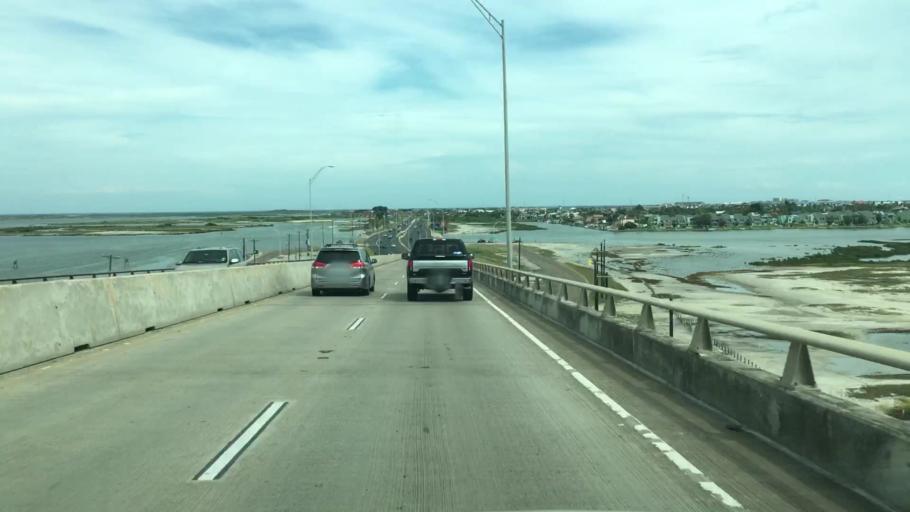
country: US
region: Texas
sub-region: Nueces County
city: Corpus Christi
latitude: 27.6338
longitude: -97.2377
